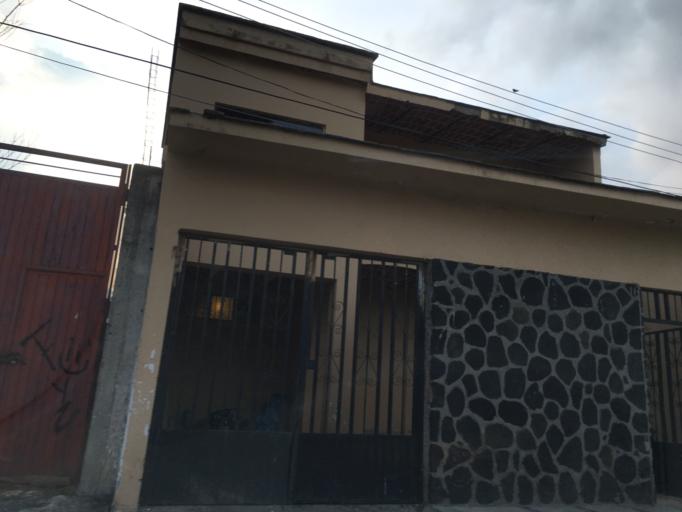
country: MX
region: Nayarit
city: Jala
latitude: 21.1001
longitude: -104.4335
